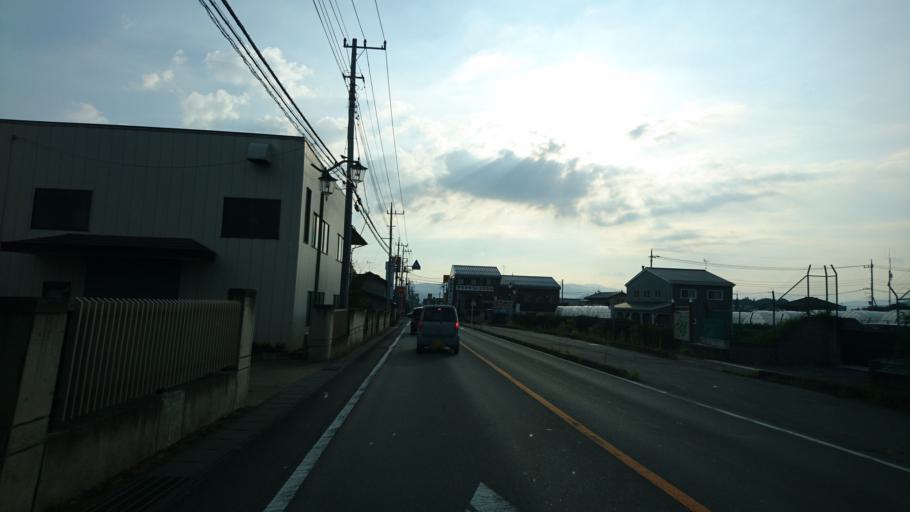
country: JP
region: Gunma
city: Numata
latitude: 36.6587
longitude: 139.0847
